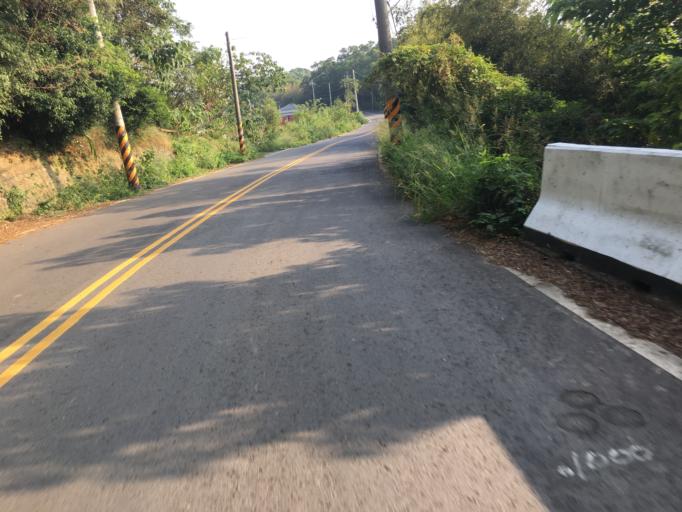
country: TW
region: Taiwan
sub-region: Hsinchu
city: Hsinchu
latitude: 24.7515
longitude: 121.0322
